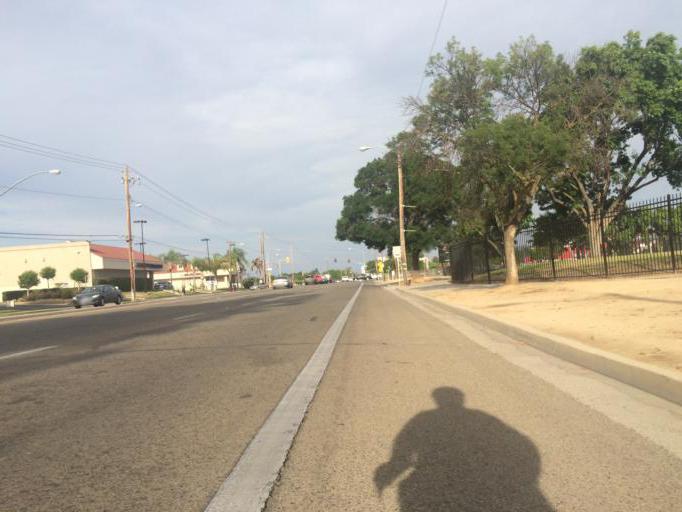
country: US
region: California
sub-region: Fresno County
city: Clovis
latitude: 36.8158
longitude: -119.7561
